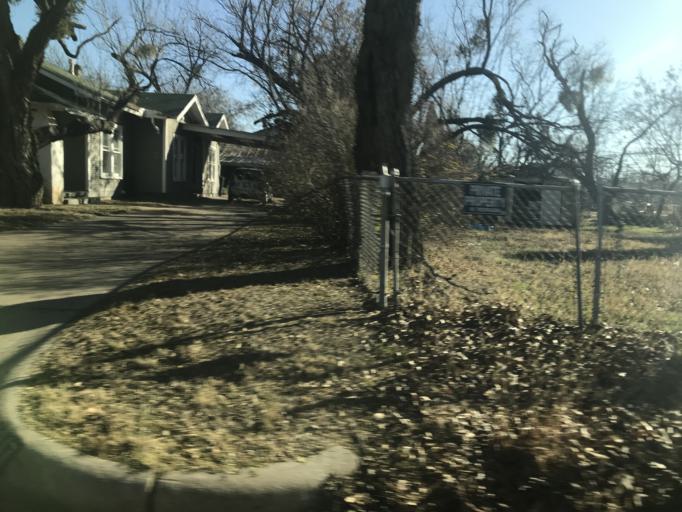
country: US
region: Texas
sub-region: Taylor County
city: Abilene
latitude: 32.4377
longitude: -99.7548
